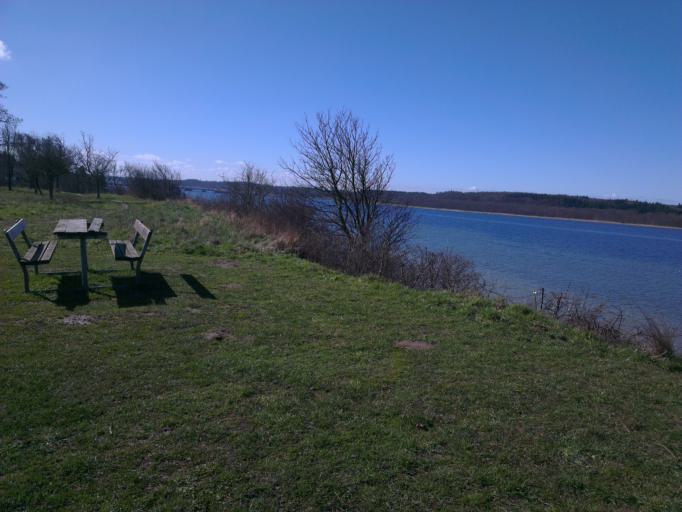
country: DK
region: Capital Region
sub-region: Frederikssund Kommune
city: Frederikssund
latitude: 55.8534
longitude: 12.0452
